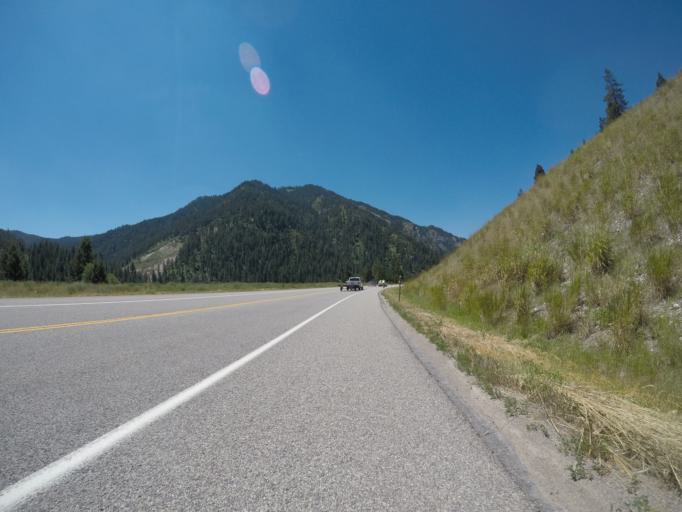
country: US
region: Wyoming
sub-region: Teton County
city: Hoback
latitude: 43.1964
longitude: -110.8726
